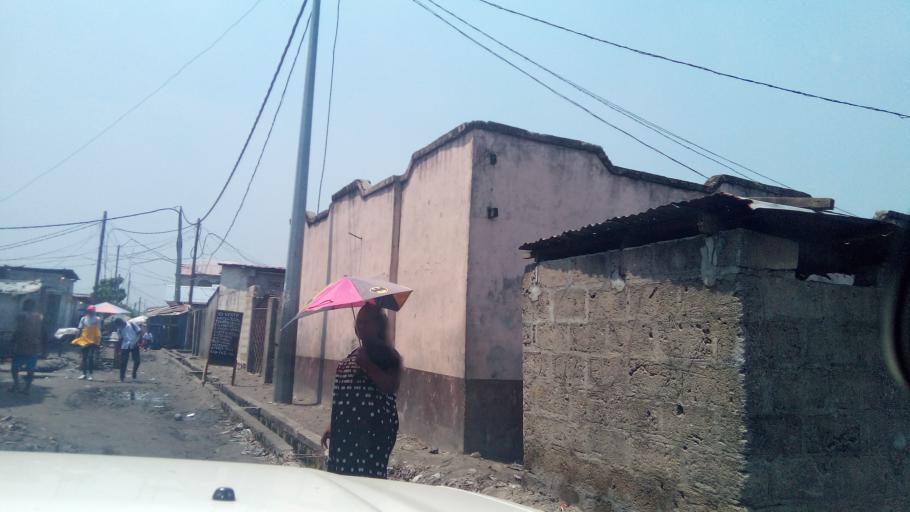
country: CD
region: Kinshasa
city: Kinshasa
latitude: -4.3706
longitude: 15.3123
